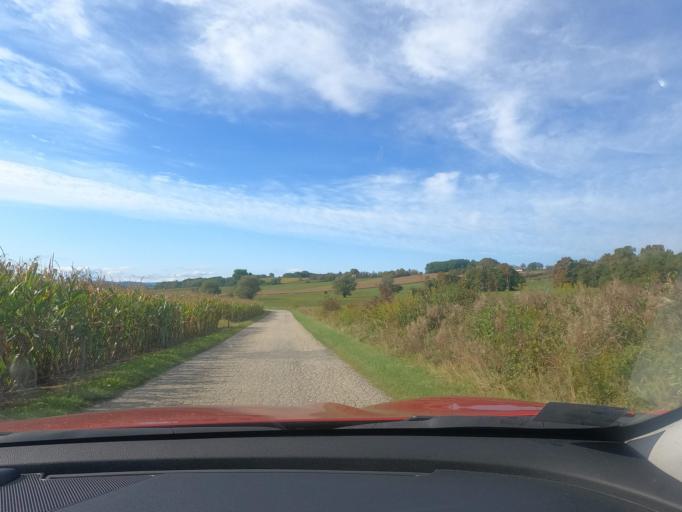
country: HR
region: Sisacko-Moslavacka
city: Petrinja
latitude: 45.3359
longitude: 16.2168
